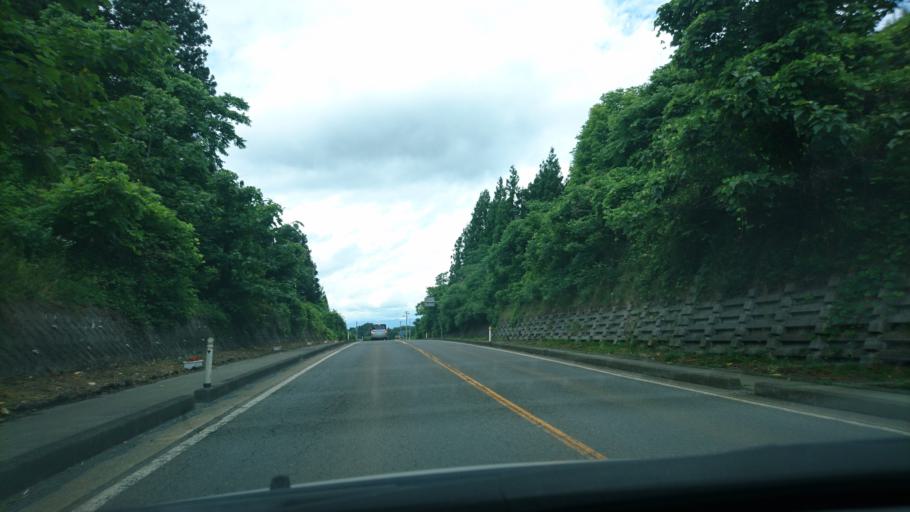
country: JP
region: Iwate
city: Morioka-shi
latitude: 39.6129
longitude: 141.2001
